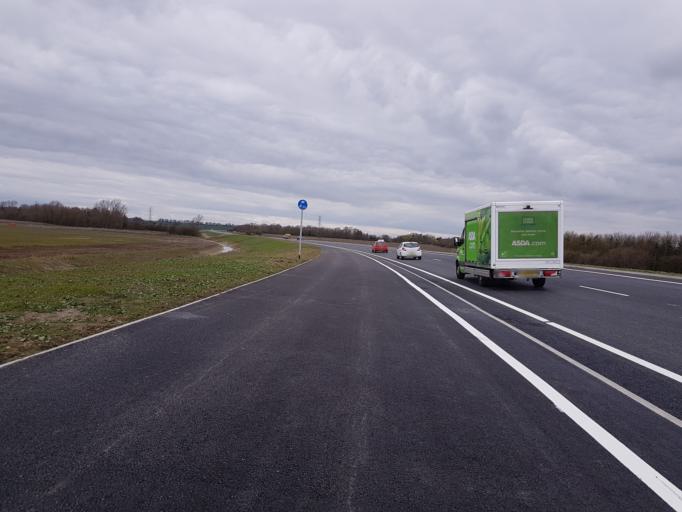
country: GB
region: England
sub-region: Cambridgeshire
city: Girton
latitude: 52.2378
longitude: 0.0563
